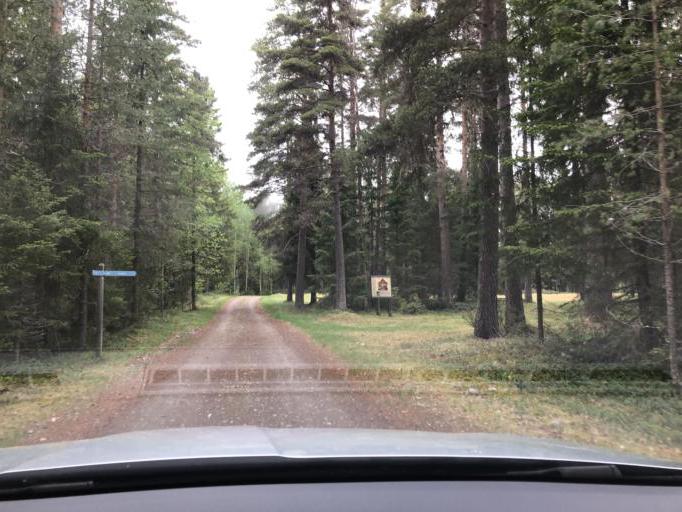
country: SE
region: Norrbotten
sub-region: Pitea Kommun
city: Roknas
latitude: 65.3941
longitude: 21.2675
